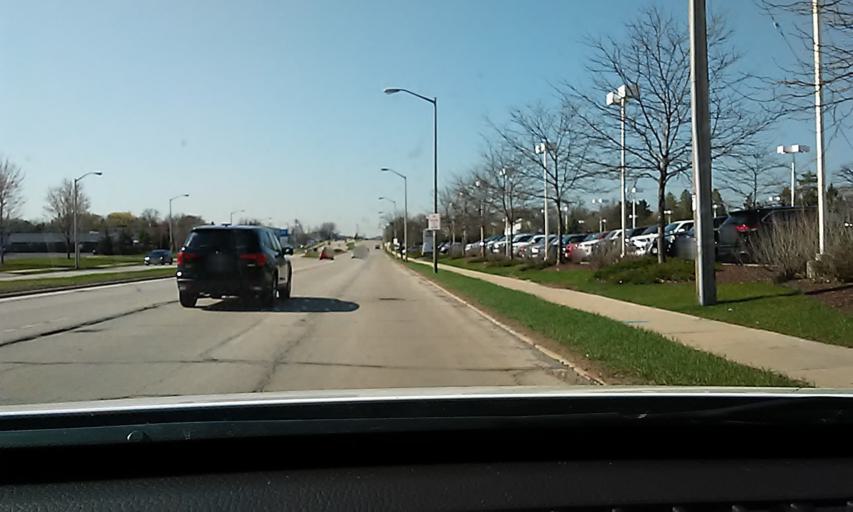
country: US
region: Wisconsin
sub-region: Milwaukee County
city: Greenfield
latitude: 42.9845
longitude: -88.0475
